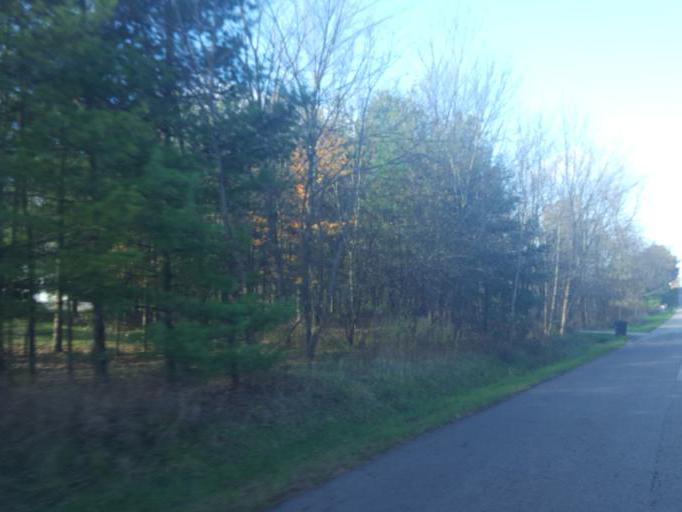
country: US
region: Ohio
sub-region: Crawford County
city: Galion
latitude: 40.6389
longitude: -82.7357
